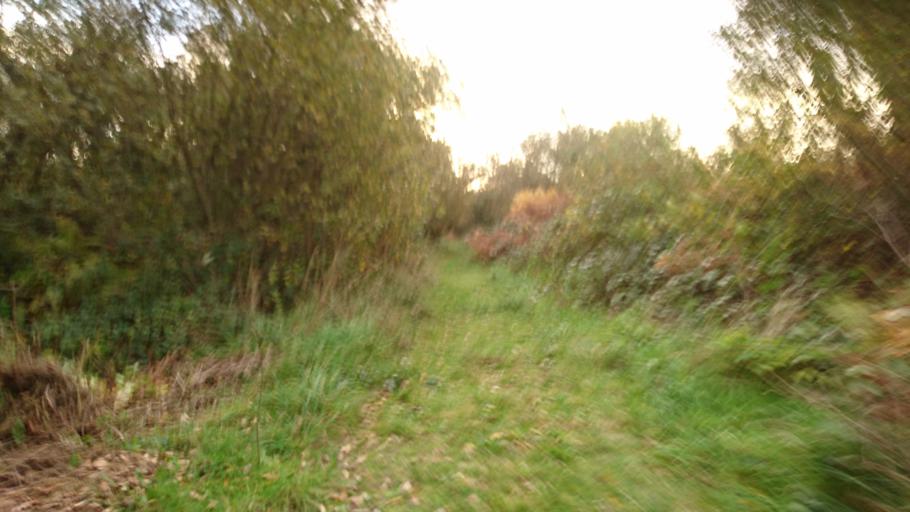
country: FR
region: Brittany
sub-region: Departement du Finistere
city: Lampaul-Plouarzel
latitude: 48.4379
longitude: -4.7704
